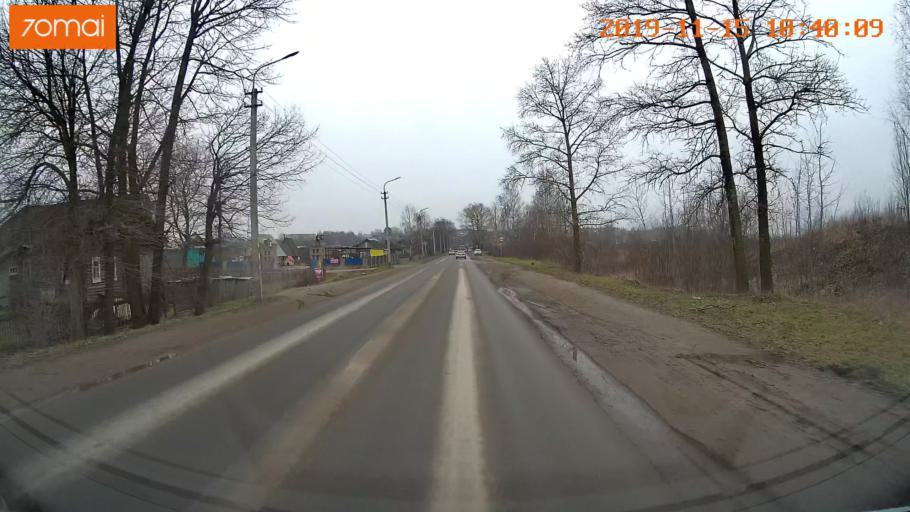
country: RU
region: Vologda
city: Sheksna
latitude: 59.2163
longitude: 38.5100
